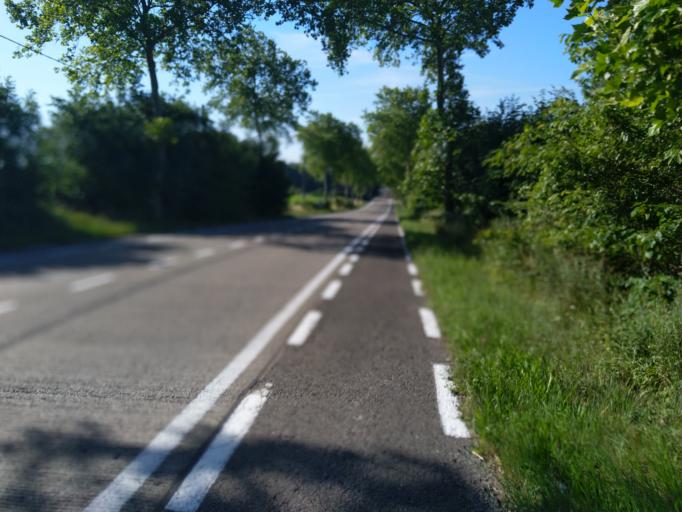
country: BE
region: Wallonia
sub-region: Province du Hainaut
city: Chasse Royale
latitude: 50.4120
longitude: 3.9564
